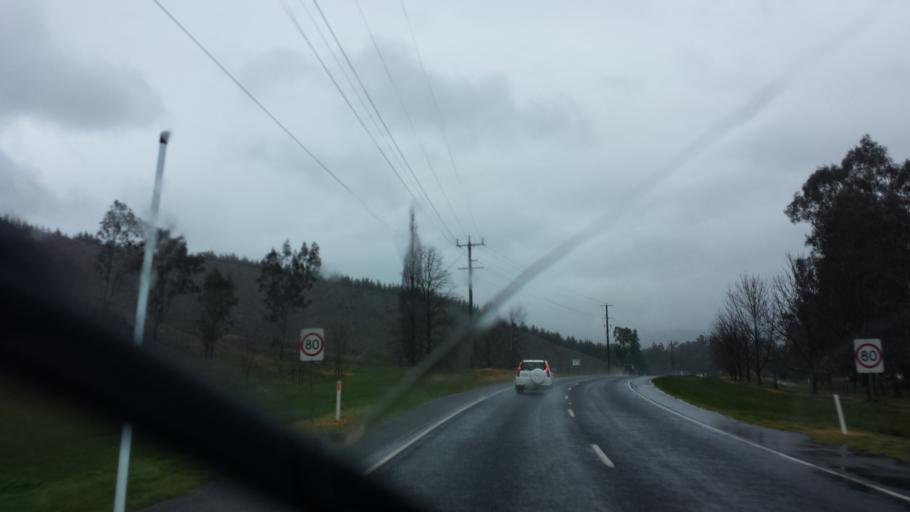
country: AU
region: Victoria
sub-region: Alpine
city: Mount Beauty
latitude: -36.5766
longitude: 146.7487
